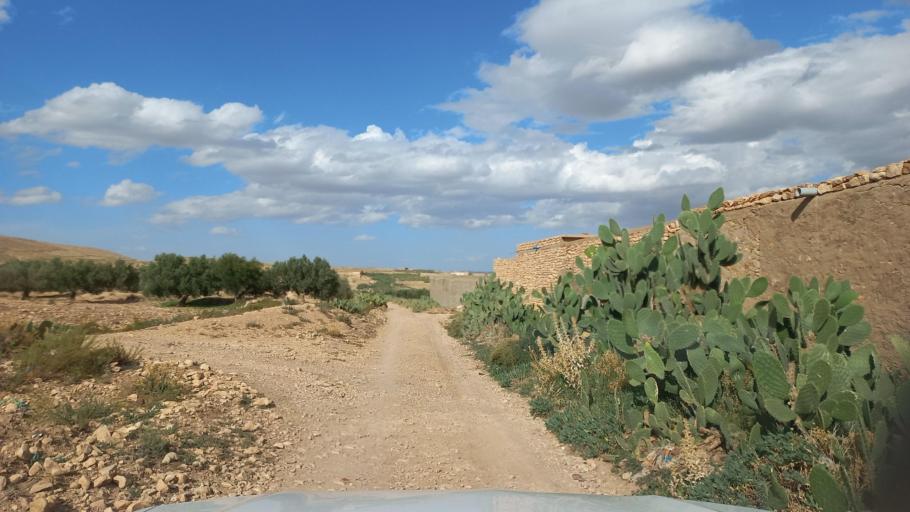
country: TN
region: Al Qasrayn
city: Sbiba
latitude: 35.4521
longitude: 9.0731
